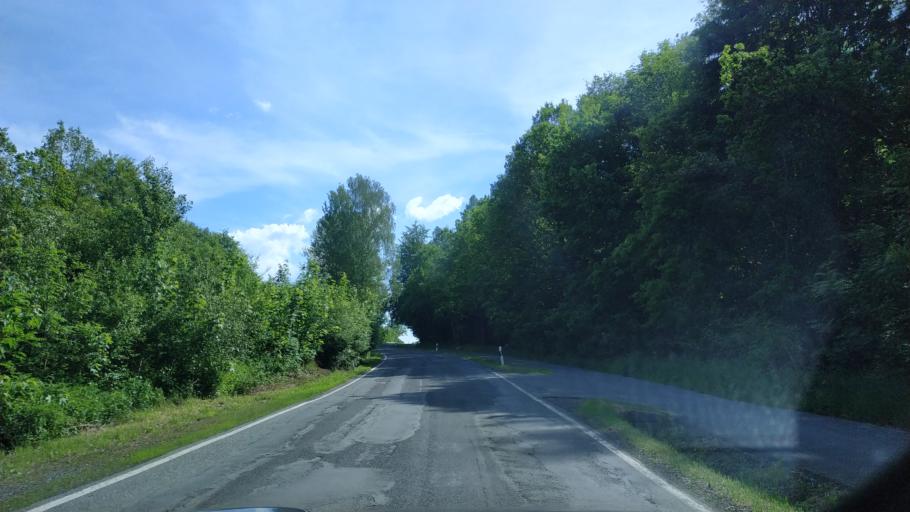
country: DE
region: Saxony
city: Plauen
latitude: 50.5302
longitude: 12.1344
